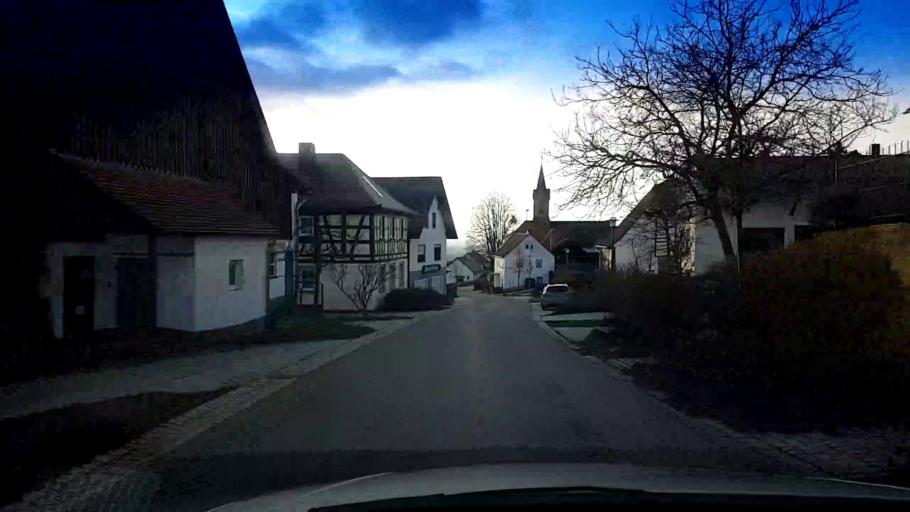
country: DE
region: Bavaria
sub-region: Upper Franconia
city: Buttenheim
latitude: 49.8411
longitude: 11.0377
